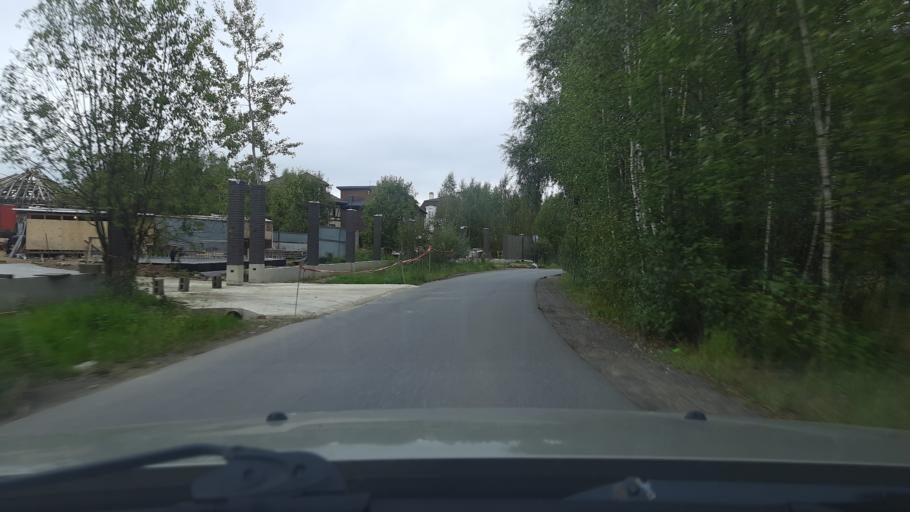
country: RU
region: Moskovskaya
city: Barvikha
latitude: 55.7271
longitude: 37.3001
